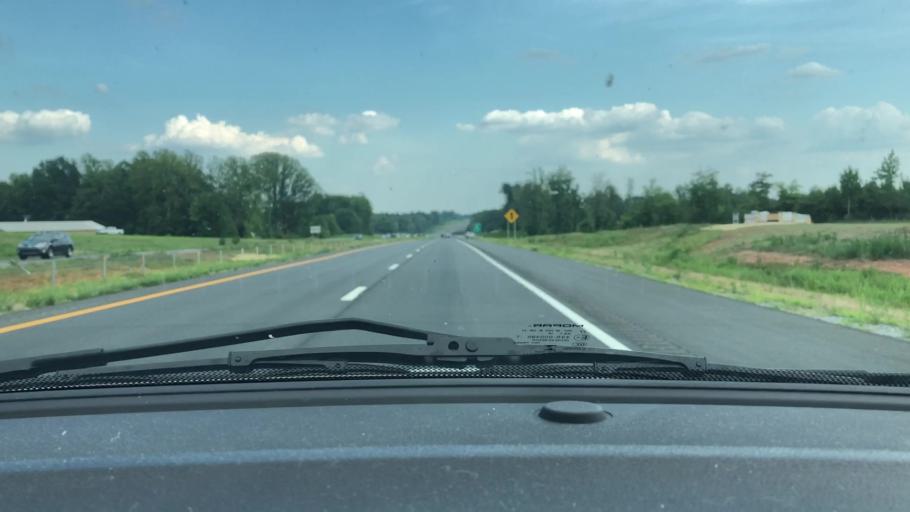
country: US
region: North Carolina
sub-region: Guilford County
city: Stokesdale
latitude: 36.2670
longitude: -79.9304
